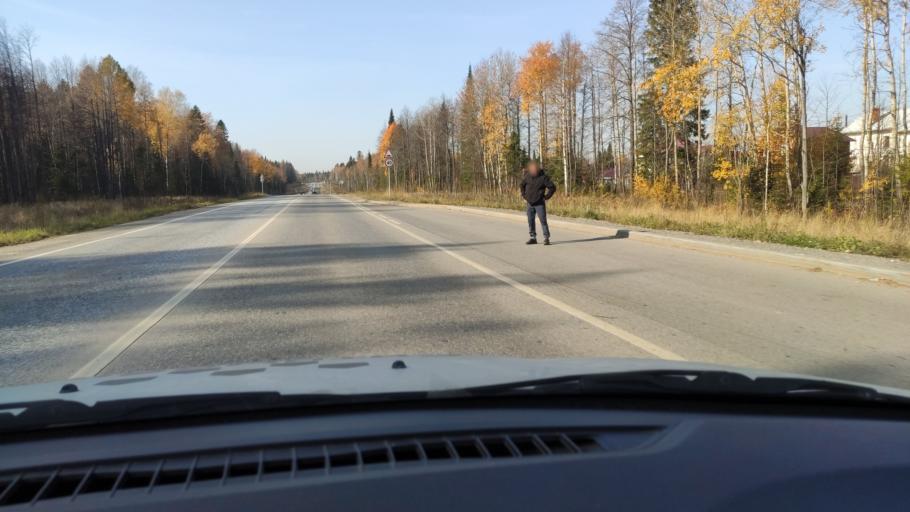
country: RU
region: Perm
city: Novyye Lyady
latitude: 58.0484
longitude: 56.5683
